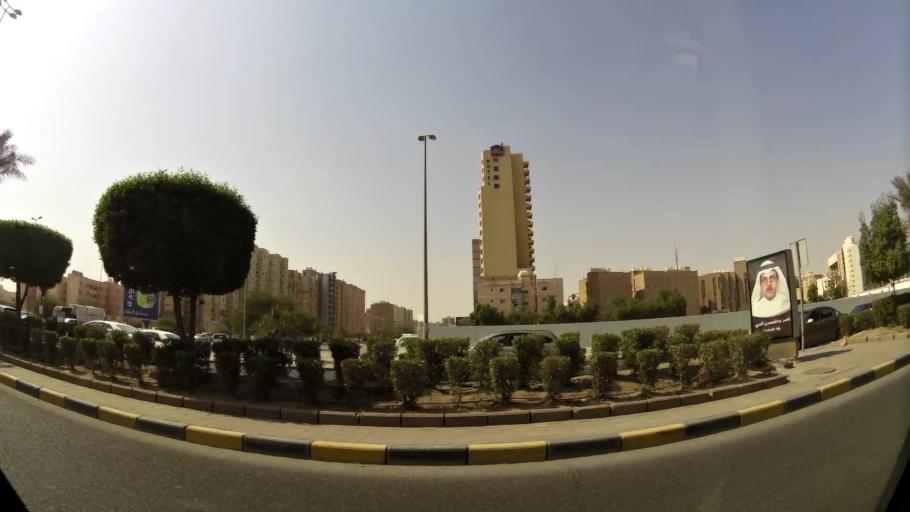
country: KW
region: Al Ahmadi
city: Al Mahbulah
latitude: 29.1385
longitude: 48.1301
